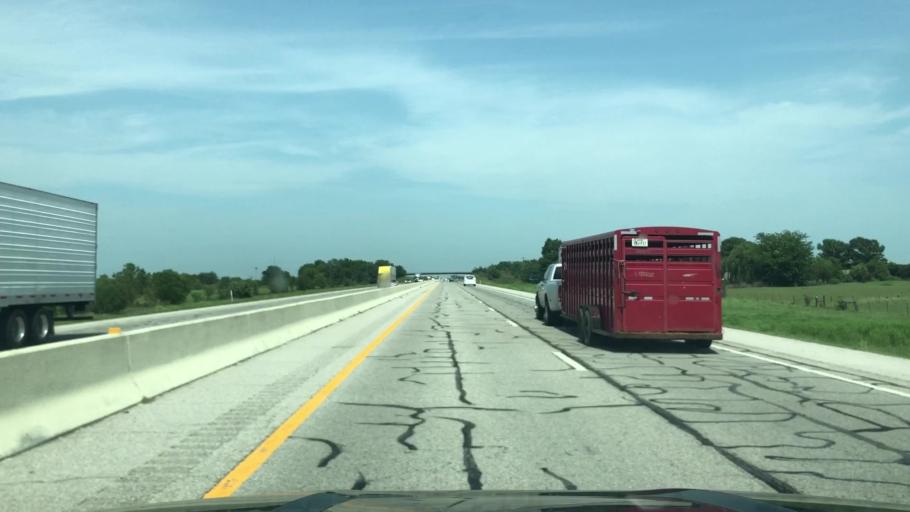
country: US
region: Oklahoma
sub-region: Craig County
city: Vinita
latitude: 36.5202
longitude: -95.2594
